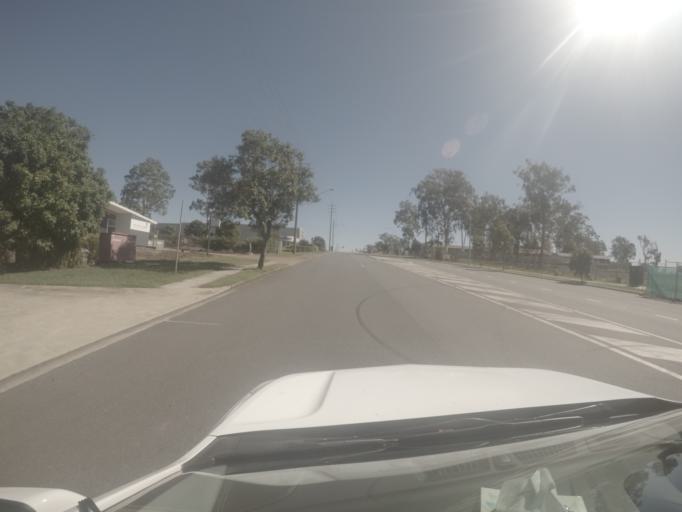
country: AU
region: Queensland
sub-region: Brisbane
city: Wacol
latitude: -27.5835
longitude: 152.9440
